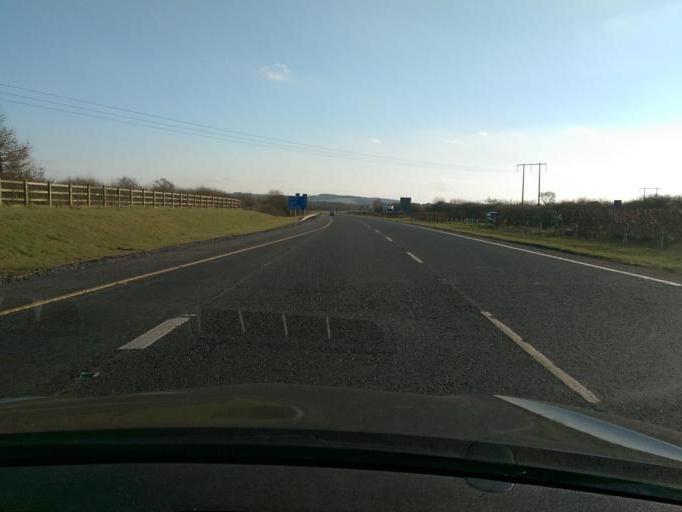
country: IE
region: Leinster
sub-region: Laois
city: Portlaoise
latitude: 53.0433
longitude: -7.2432
